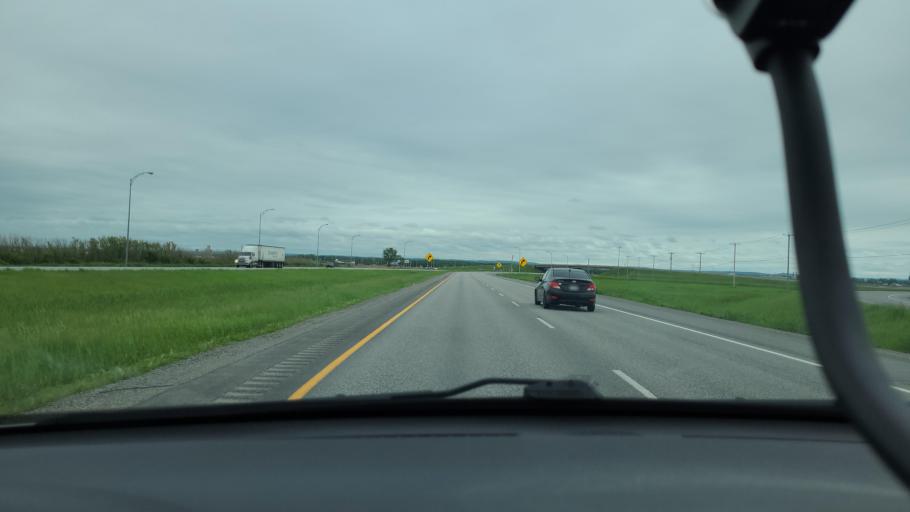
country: CA
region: Quebec
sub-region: Lanaudiere
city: Sainte-Julienne
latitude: 45.8811
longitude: -73.6560
